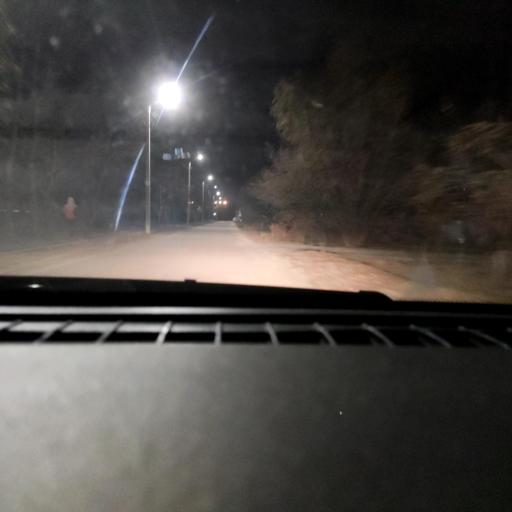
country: RU
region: Voronezj
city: Voronezh
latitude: 51.6312
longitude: 39.1610
